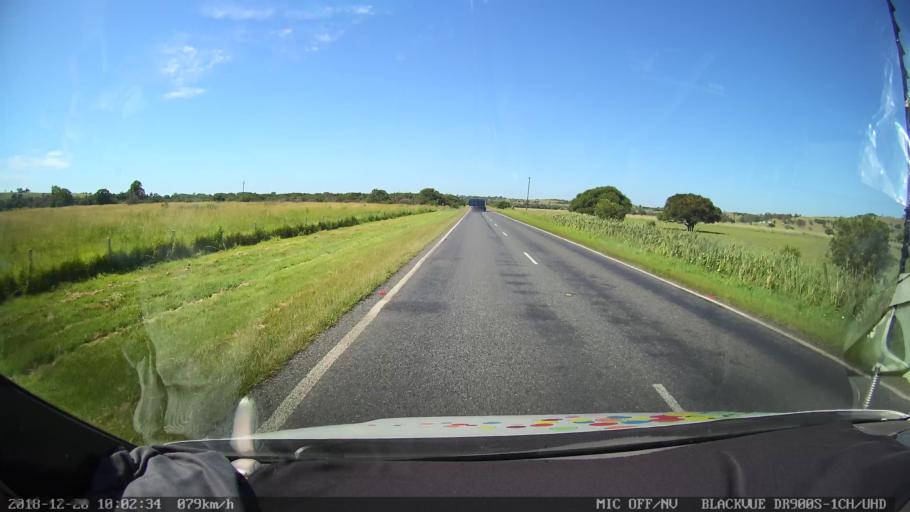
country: AU
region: New South Wales
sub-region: Lismore Municipality
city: East Lismore
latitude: -28.8595
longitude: 153.2613
